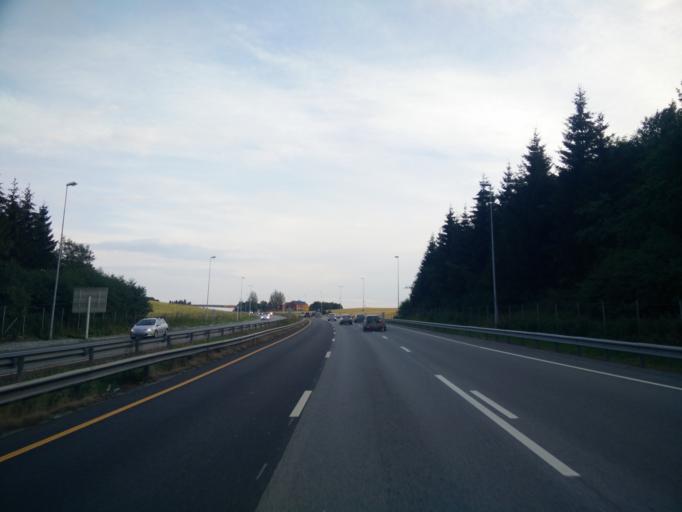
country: NO
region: Sor-Trondelag
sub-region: Trondheim
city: Trondheim
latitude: 63.3800
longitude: 10.3746
